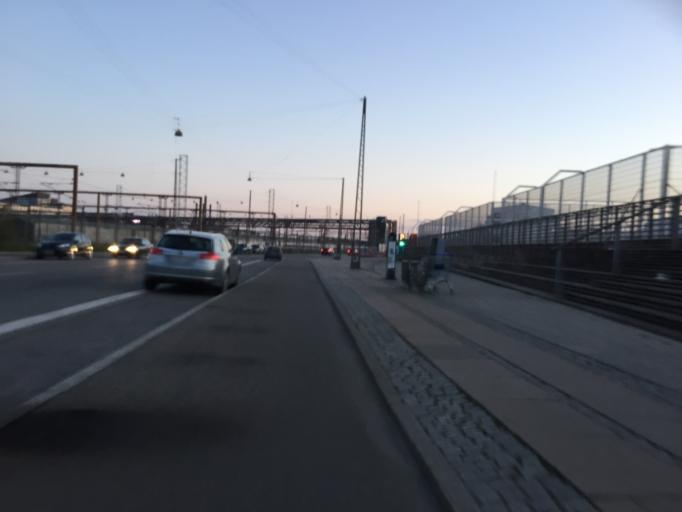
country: DK
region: Capital Region
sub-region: Kobenhavn
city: Copenhagen
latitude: 55.6684
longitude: 12.5645
